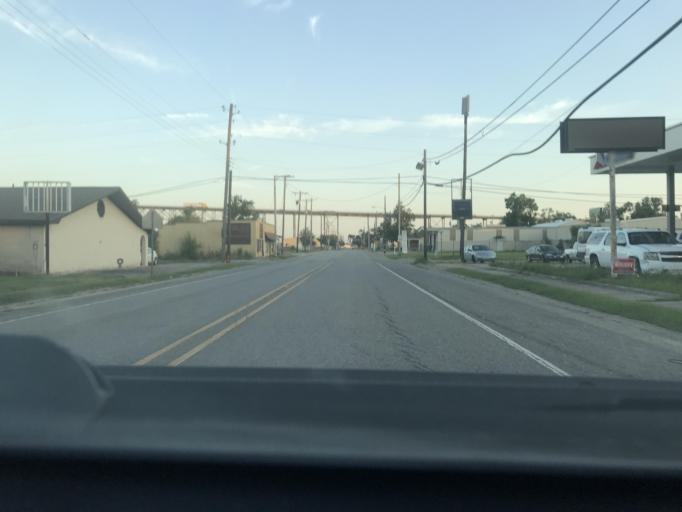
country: US
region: Louisiana
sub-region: Calcasieu Parish
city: Westlake
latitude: 30.2417
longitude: -93.2506
